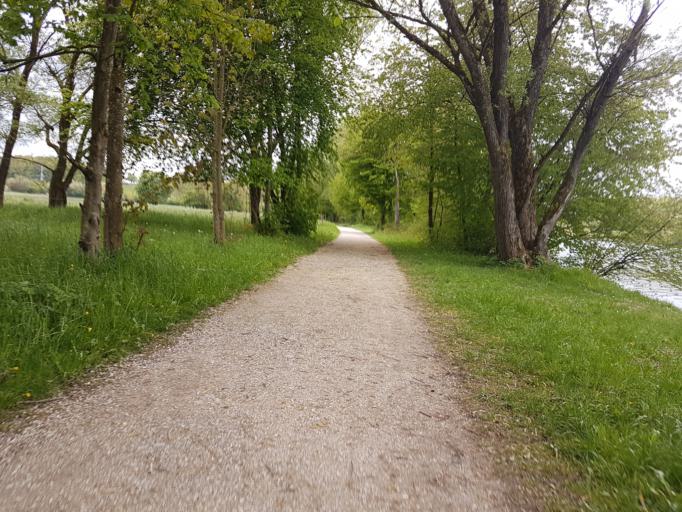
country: CH
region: Bern
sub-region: Oberaargau
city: Herzogenbuchsee
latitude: 47.2266
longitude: 7.7262
